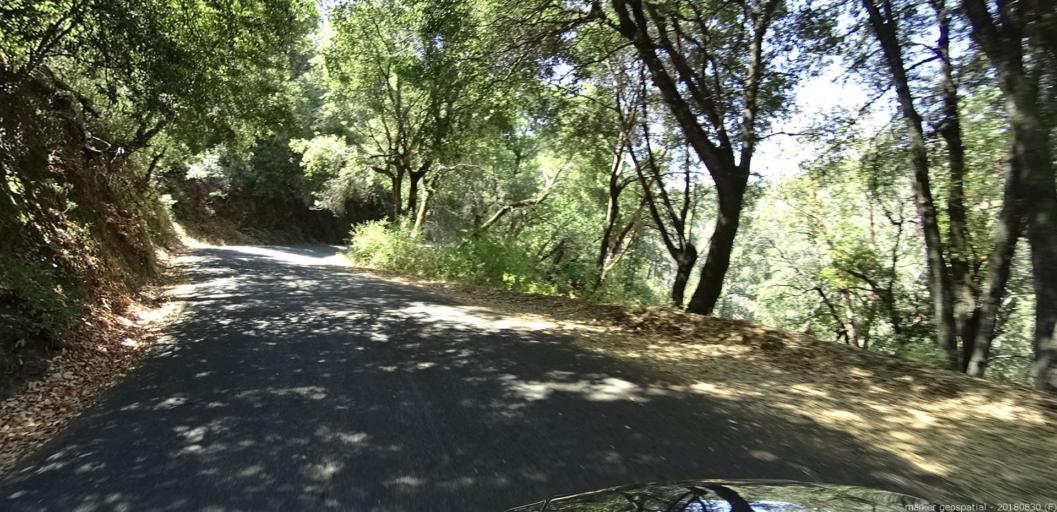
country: US
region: California
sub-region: Monterey County
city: Greenfield
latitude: 36.0115
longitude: -121.4460
